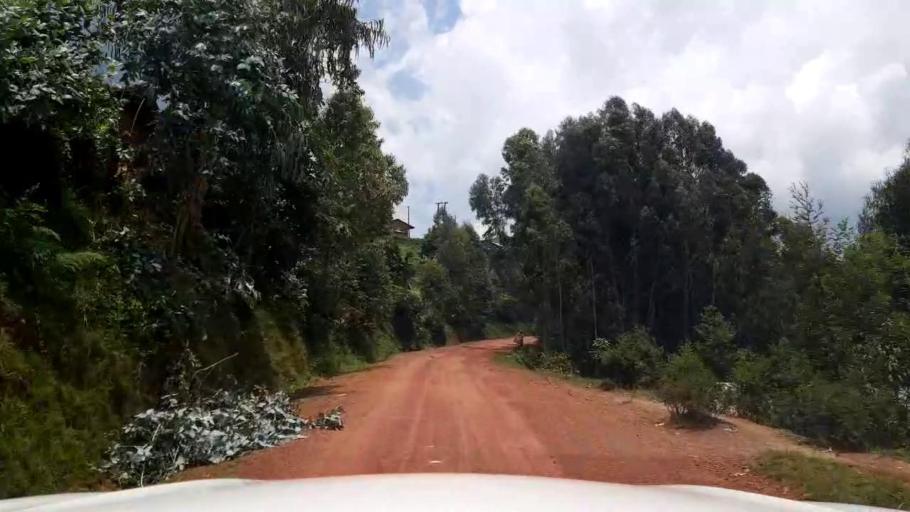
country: RW
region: Northern Province
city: Byumba
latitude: -1.4940
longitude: 29.9306
